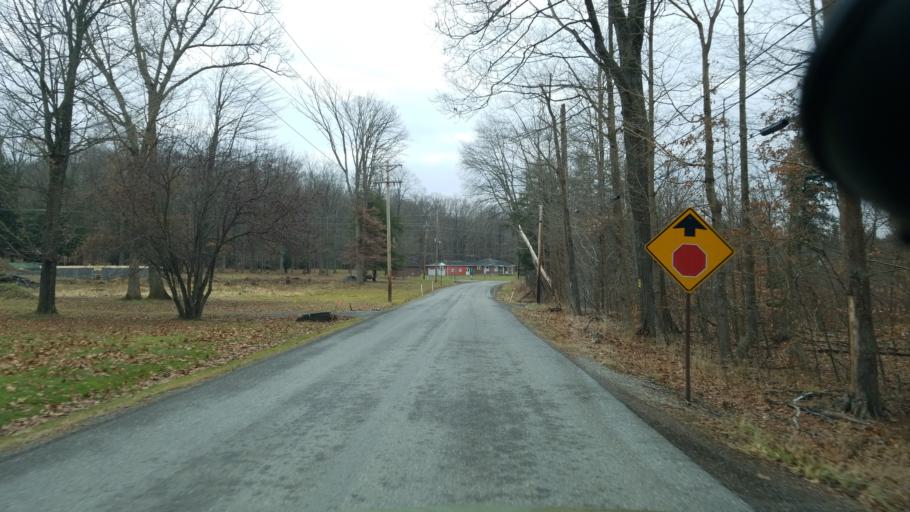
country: US
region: Pennsylvania
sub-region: Clearfield County
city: DuBois
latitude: 41.1105
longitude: -78.6944
